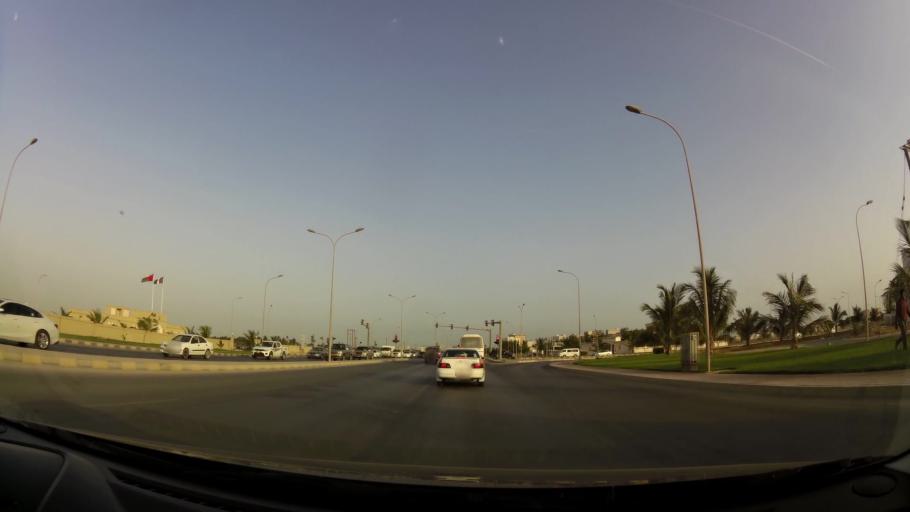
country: OM
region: Zufar
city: Salalah
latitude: 17.0135
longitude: 54.0365
